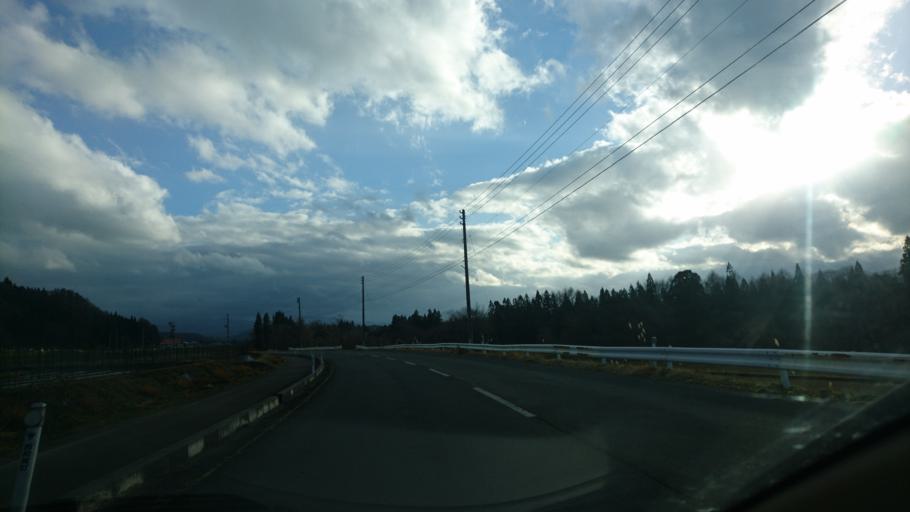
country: JP
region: Akita
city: Yokotemachi
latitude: 39.3864
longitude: 140.7648
